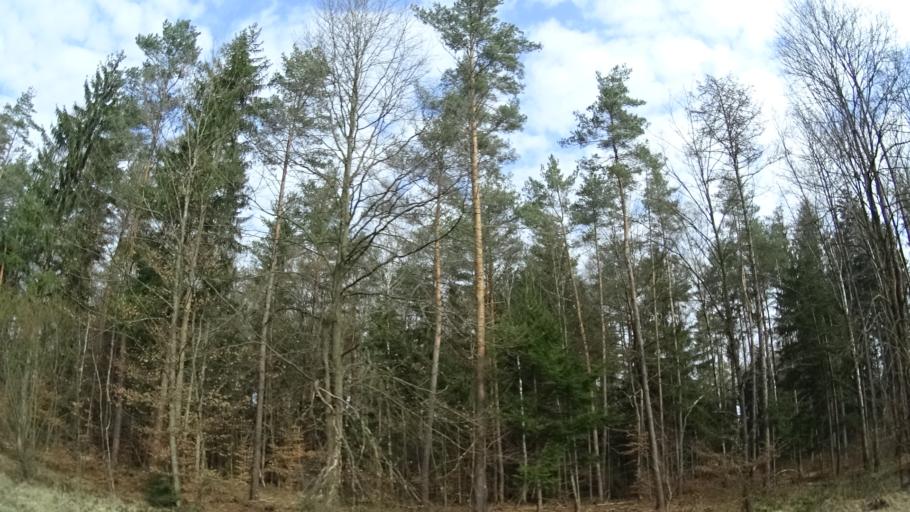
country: DE
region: Bavaria
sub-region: Regierungsbezirk Mittelfranken
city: Winkelhaid
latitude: 49.4120
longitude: 11.2756
